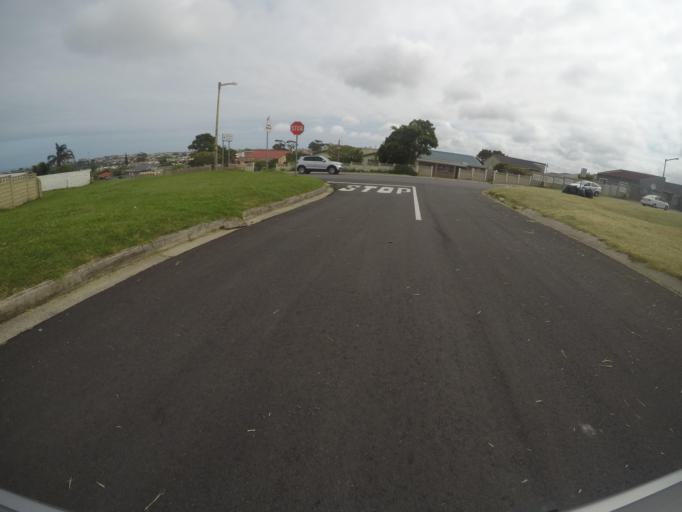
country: ZA
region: Eastern Cape
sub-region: Buffalo City Metropolitan Municipality
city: East London
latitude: -33.0004
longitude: 27.8782
